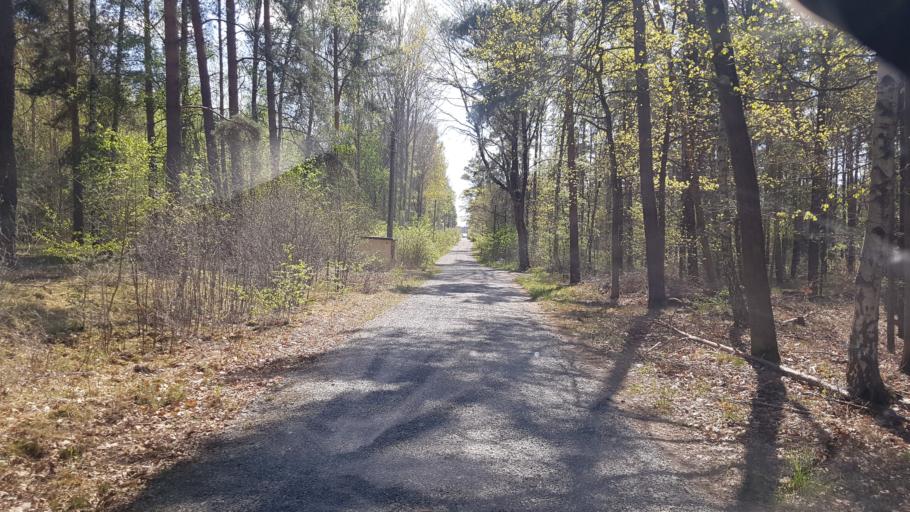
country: DE
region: Brandenburg
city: Crinitz
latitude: 51.7484
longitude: 13.7702
